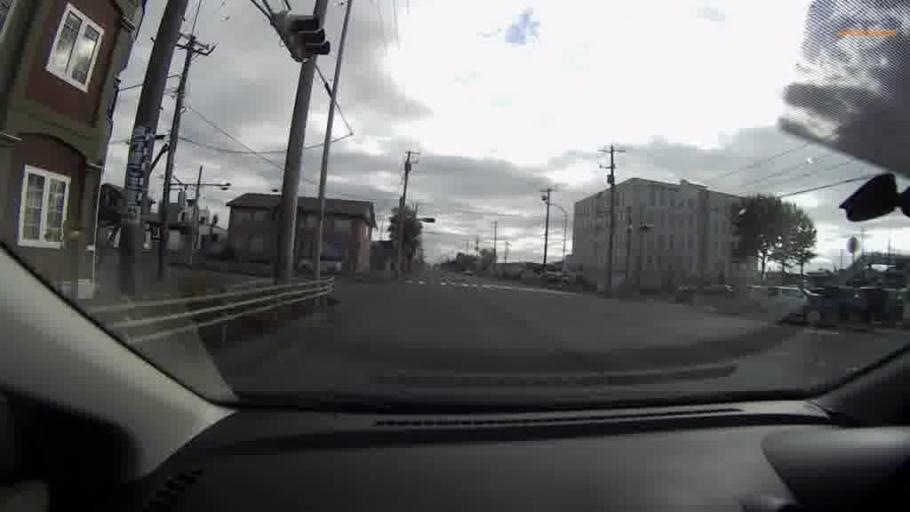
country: JP
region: Hokkaido
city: Kushiro
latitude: 43.0099
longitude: 144.2724
